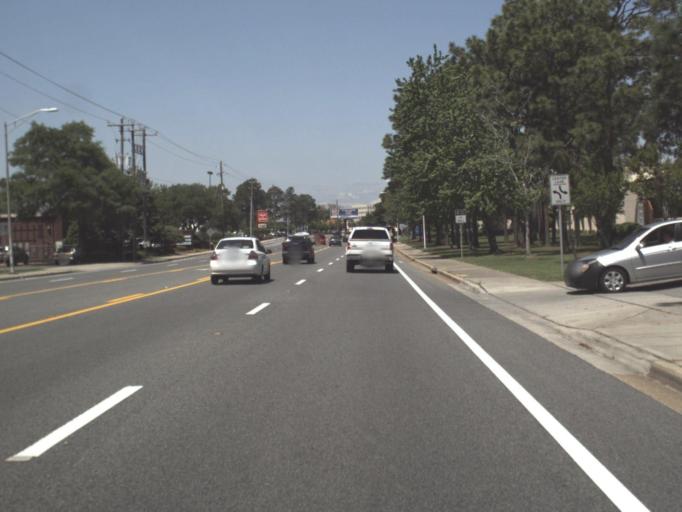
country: US
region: Florida
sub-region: Escambia County
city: Brent
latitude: 30.4765
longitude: -87.2028
